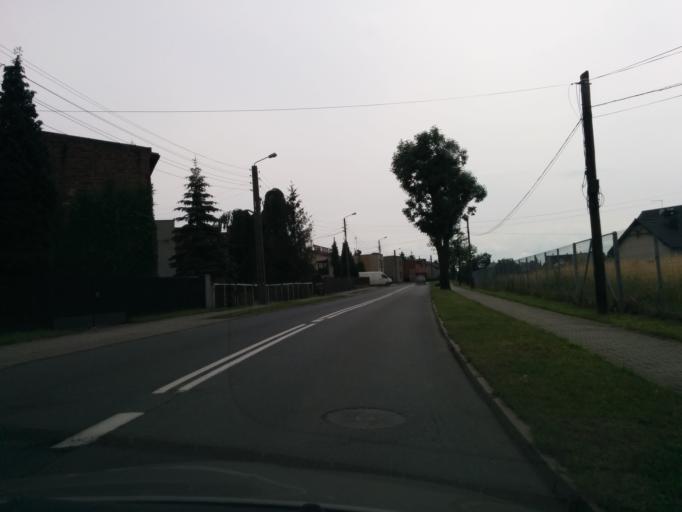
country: PL
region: Silesian Voivodeship
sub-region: Ruda Slaska
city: Ruda Slaska
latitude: 50.2533
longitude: 18.8393
